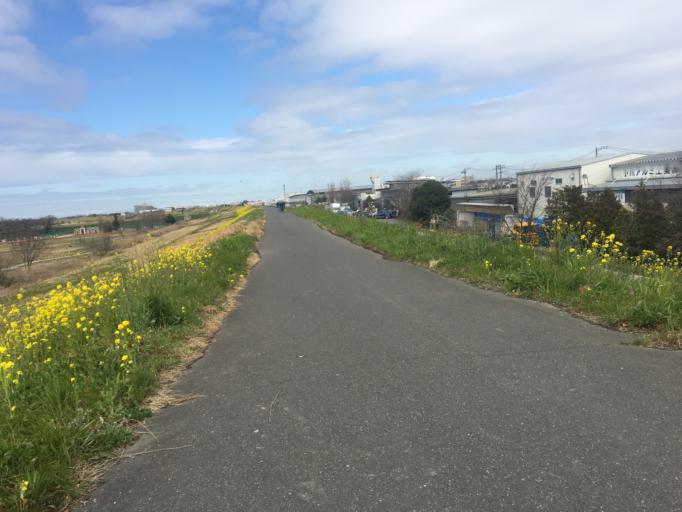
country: JP
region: Saitama
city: Shiki
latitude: 35.8488
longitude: 139.6127
